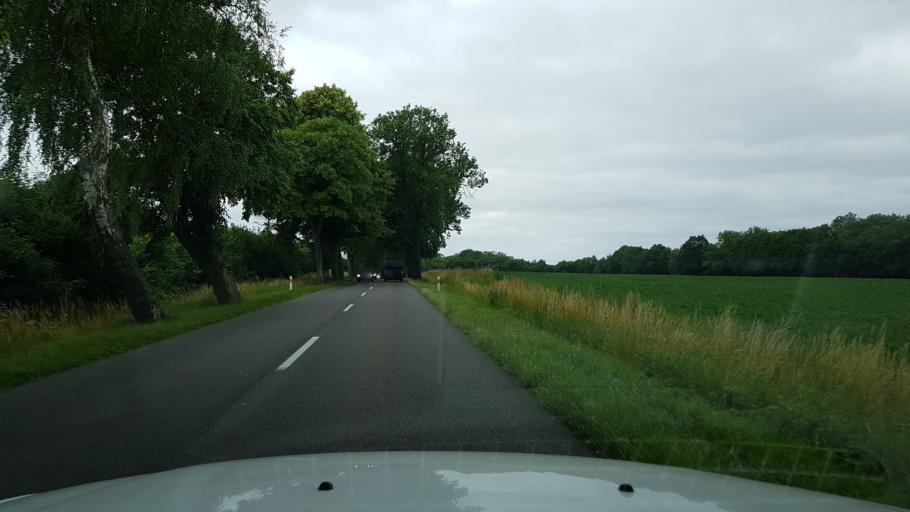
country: PL
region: West Pomeranian Voivodeship
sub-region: Powiat kamienski
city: Kamien Pomorski
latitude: 53.9610
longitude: 14.8027
